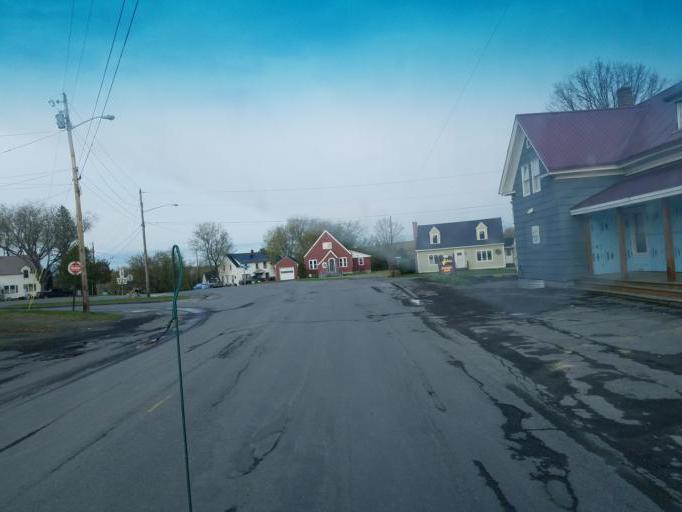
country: US
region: Maine
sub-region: Aroostook County
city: Caribou
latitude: 46.8605
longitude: -68.0059
